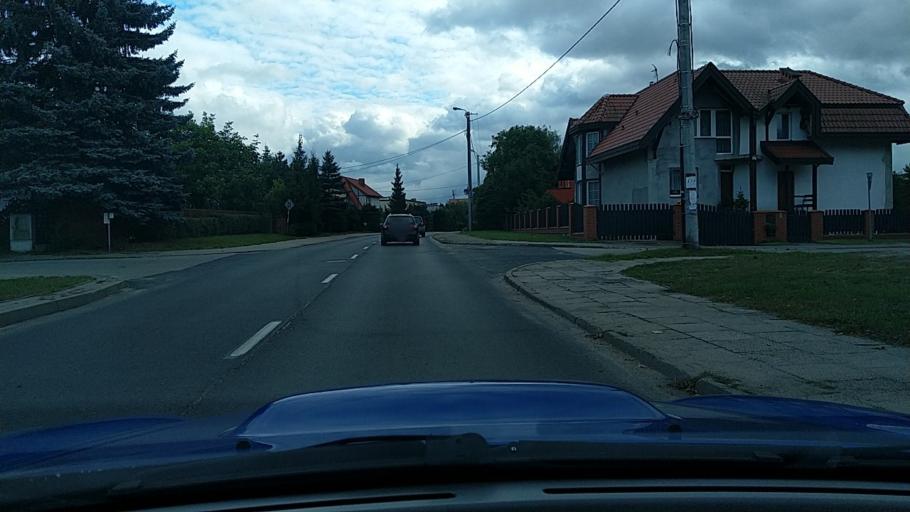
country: PL
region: Warmian-Masurian Voivodeship
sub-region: Olsztyn
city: Kortowo
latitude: 53.7678
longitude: 20.4276
